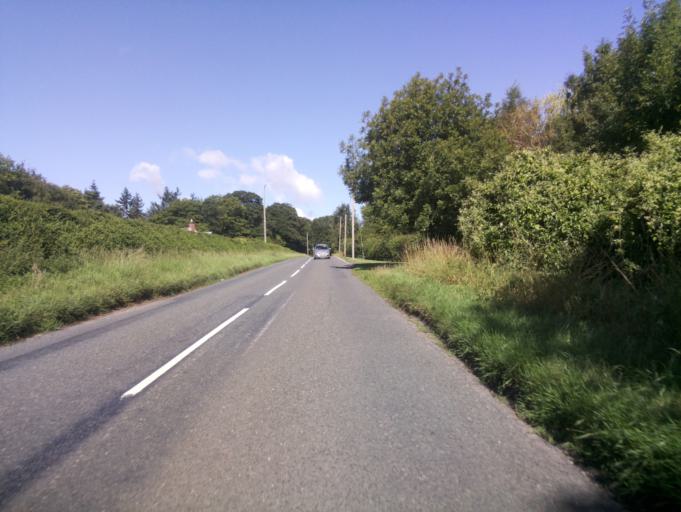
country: GB
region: England
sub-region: Herefordshire
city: Linton
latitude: 51.9345
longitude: -2.5053
